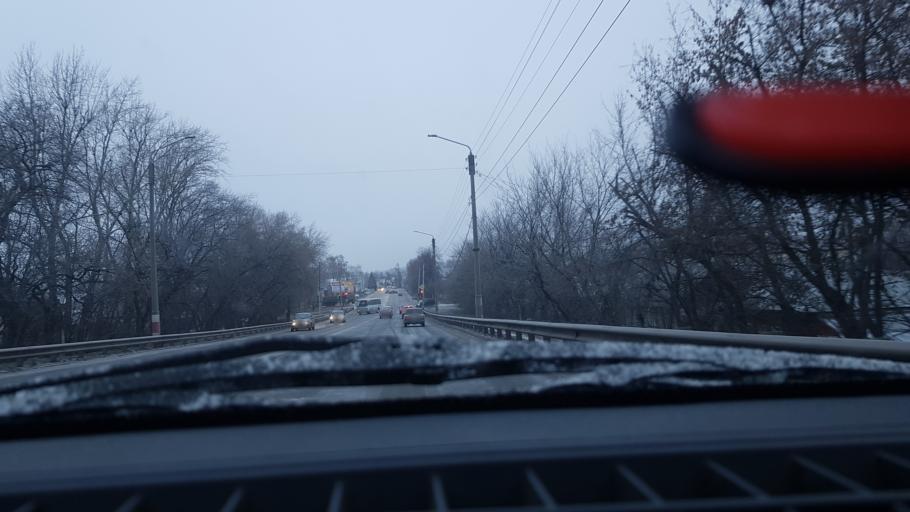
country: RU
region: Ulyanovsk
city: Dimitrovgrad
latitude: 54.2087
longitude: 49.6271
